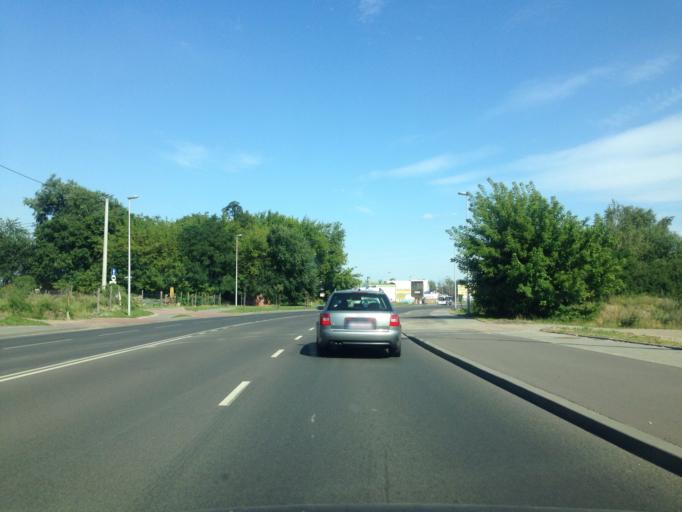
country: PL
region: Kujawsko-Pomorskie
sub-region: Torun
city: Torun
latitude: 53.0377
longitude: 18.6177
